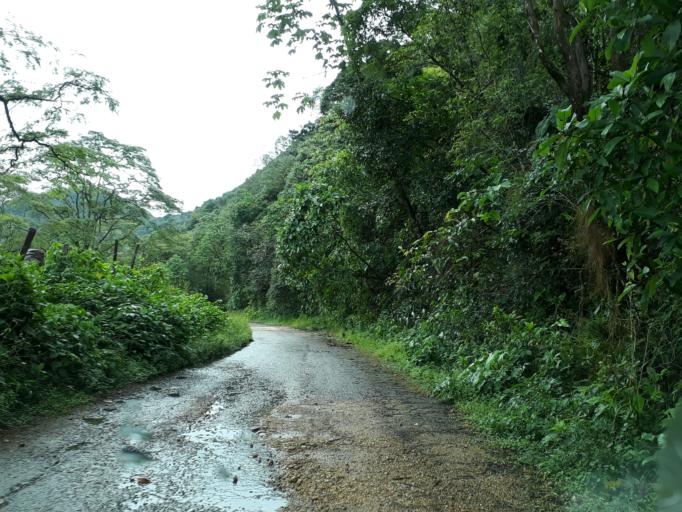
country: CO
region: Cundinamarca
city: Medina
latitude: 4.6784
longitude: -73.3196
